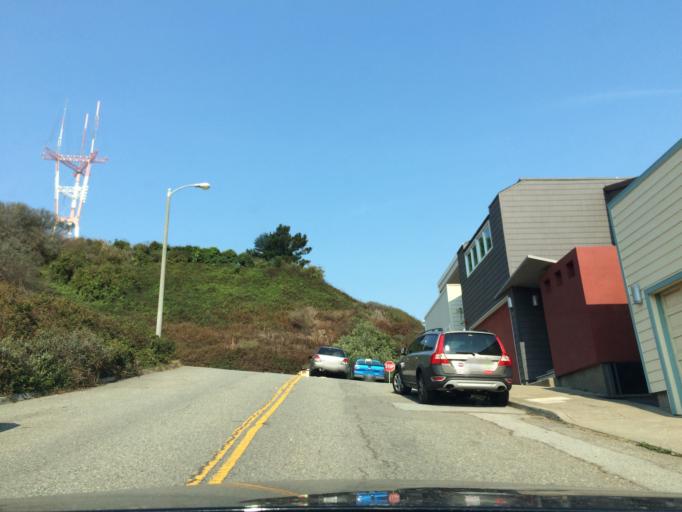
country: US
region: California
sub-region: San Francisco County
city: San Francisco
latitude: 37.7565
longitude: -122.4463
